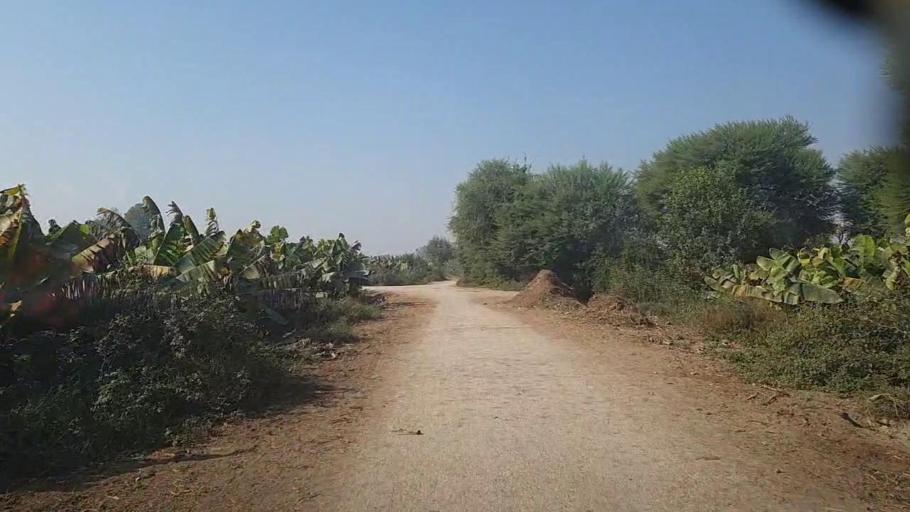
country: PK
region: Sindh
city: Kandiari
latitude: 27.0189
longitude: 68.5022
